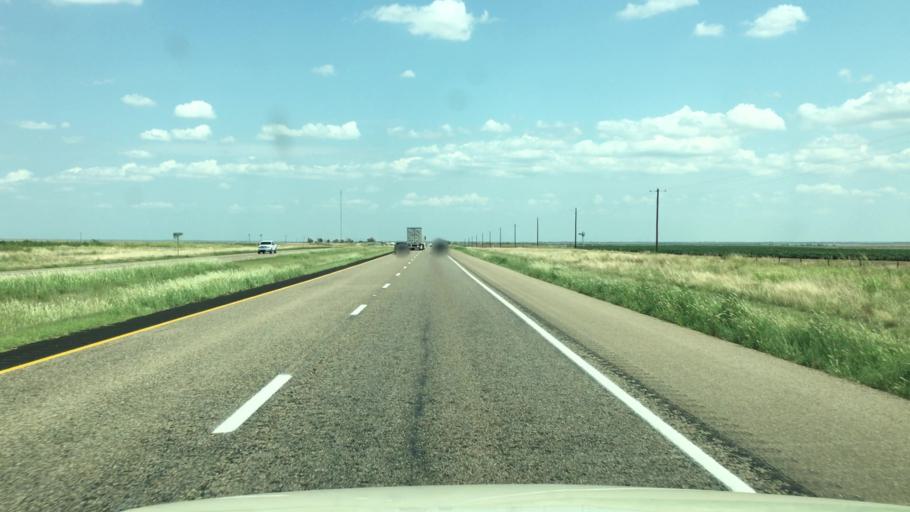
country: US
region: Texas
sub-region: Armstrong County
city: Claude
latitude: 35.0333
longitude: -101.1666
